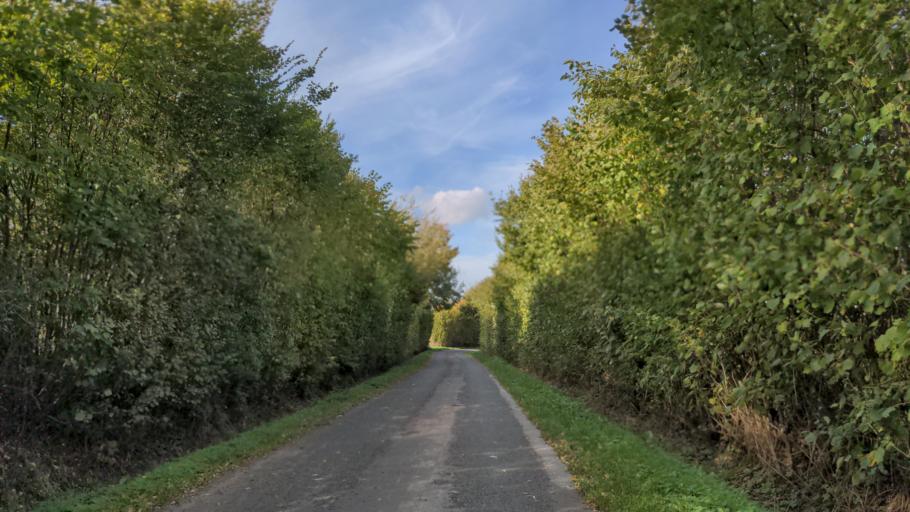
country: DE
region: Schleswig-Holstein
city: Monkhagen
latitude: 53.9283
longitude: 10.5752
